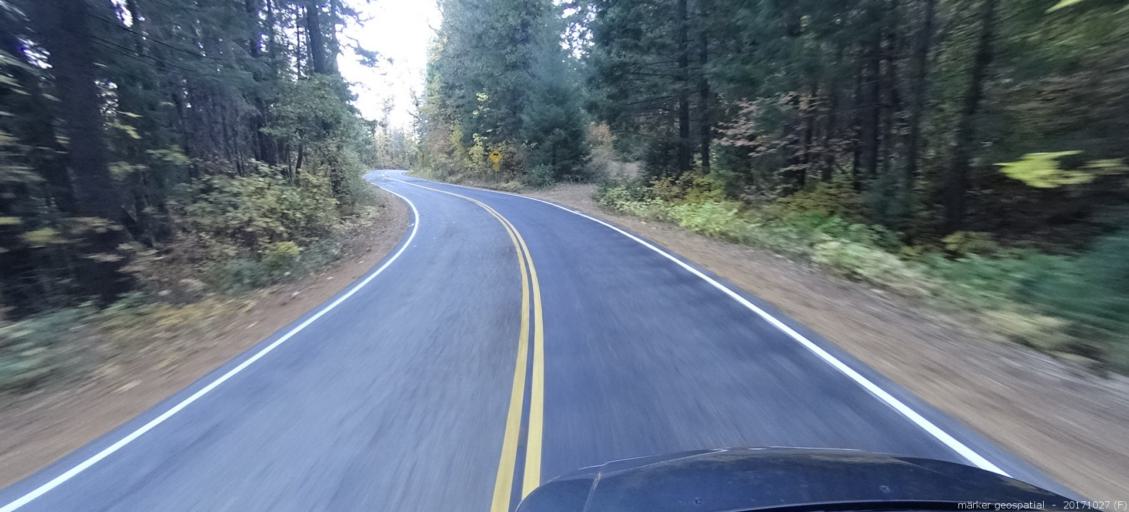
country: US
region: California
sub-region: Shasta County
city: Burney
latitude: 40.9841
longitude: -121.9276
